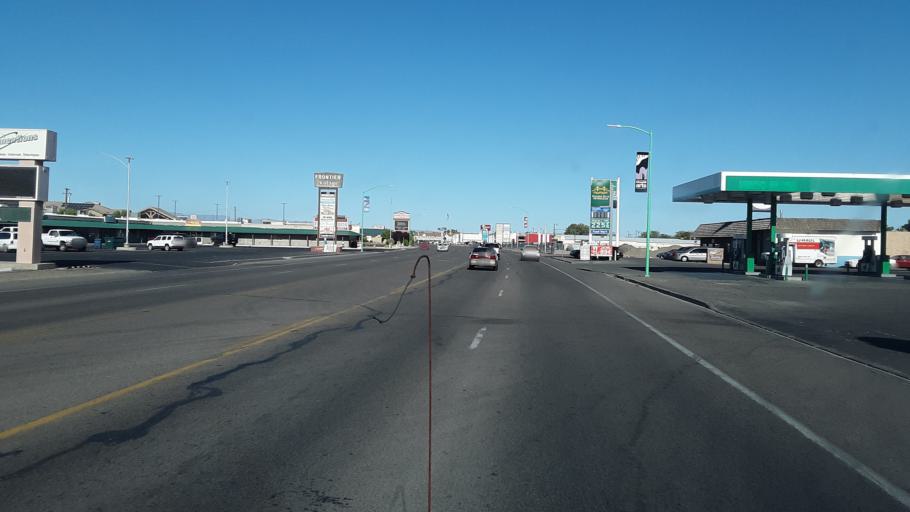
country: US
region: Nevada
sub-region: Churchill County
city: Fallon
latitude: 39.4754
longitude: -118.7974
